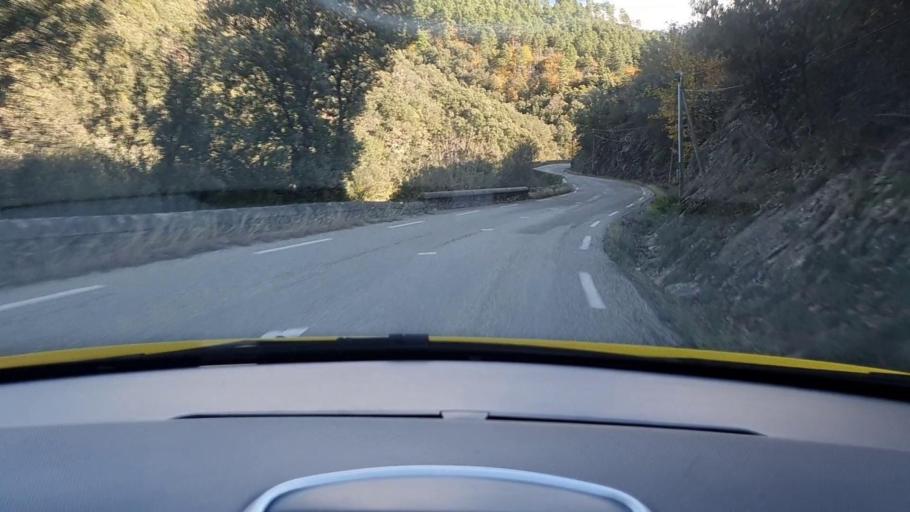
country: FR
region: Languedoc-Roussillon
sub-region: Departement du Gard
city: Valleraugue
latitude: 44.1269
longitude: 3.7391
